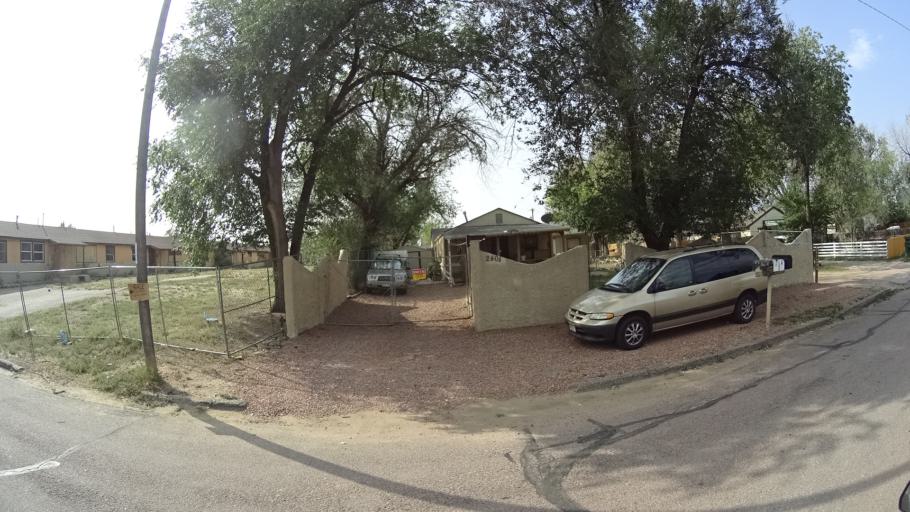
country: US
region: Colorado
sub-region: El Paso County
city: Colorado Springs
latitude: 38.8398
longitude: -104.7857
